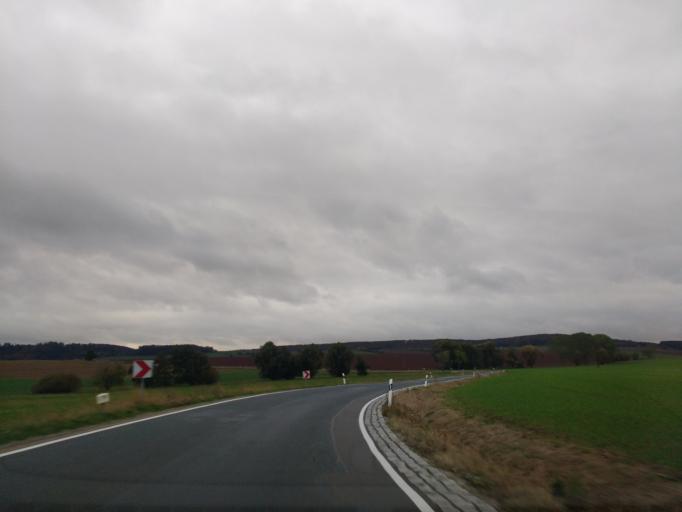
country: DE
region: Thuringia
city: Grossbodungen
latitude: 51.5226
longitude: 10.5118
